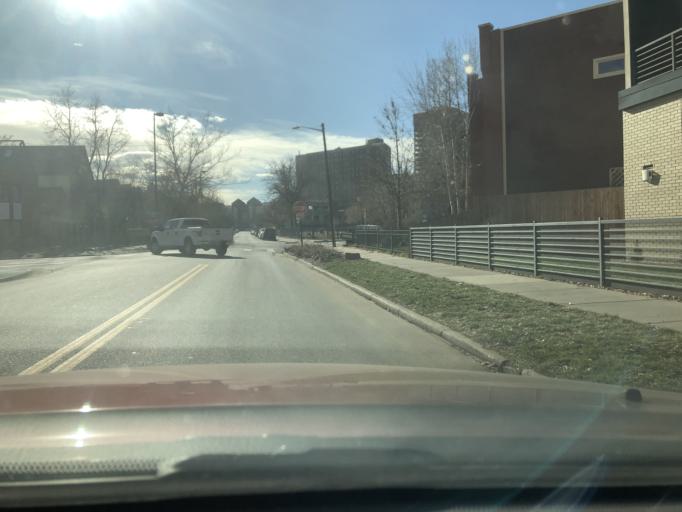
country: US
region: Colorado
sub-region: Denver County
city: Denver
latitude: 39.7511
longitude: -104.9781
